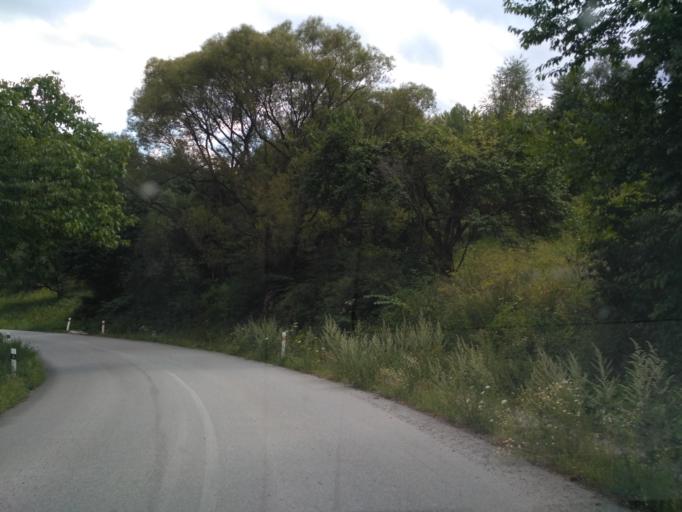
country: SK
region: Kosicky
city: Gelnica
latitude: 48.9248
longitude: 21.0489
